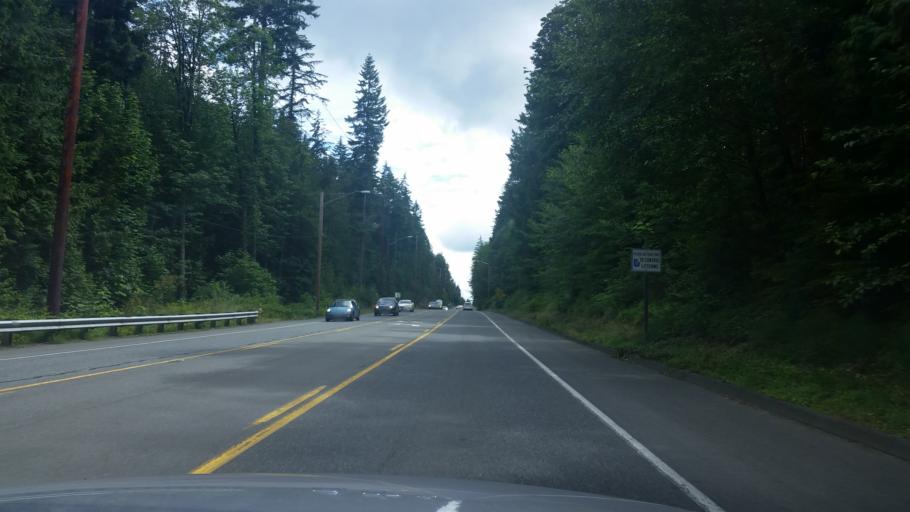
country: US
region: Washington
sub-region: King County
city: Union Hill-Novelty Hill
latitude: 47.6925
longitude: -122.0532
